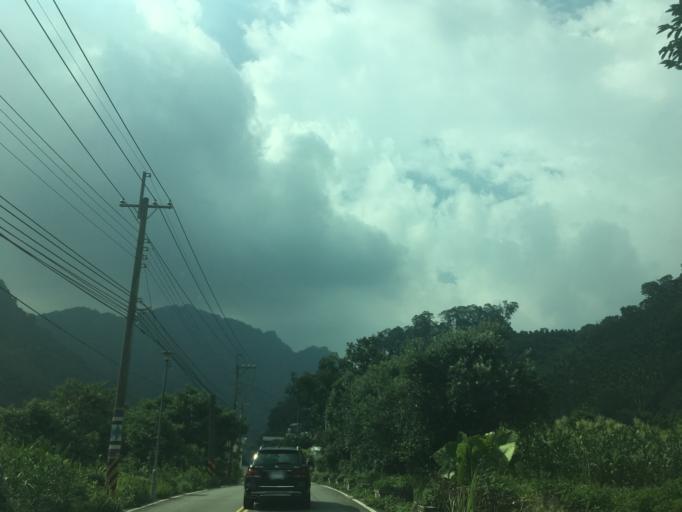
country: TW
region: Taiwan
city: Fengyuan
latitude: 24.3256
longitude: 120.9213
